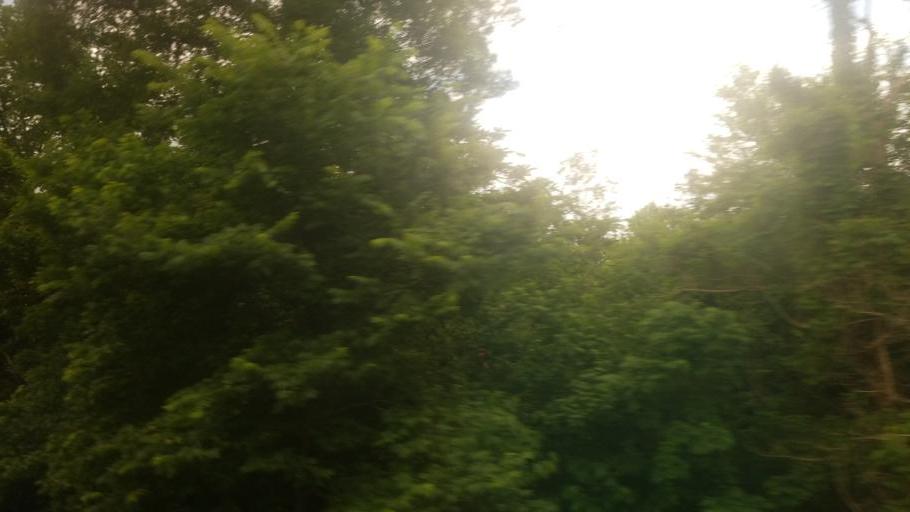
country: US
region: Maryland
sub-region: Frederick County
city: Adamstown
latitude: 39.2517
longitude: -77.4817
